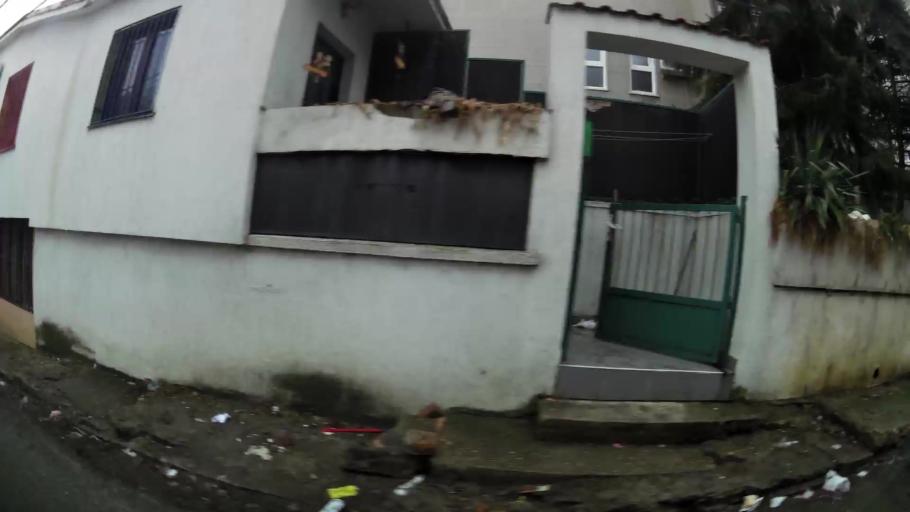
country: RS
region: Central Serbia
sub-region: Belgrade
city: Vozdovac
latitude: 44.7726
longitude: 20.4789
